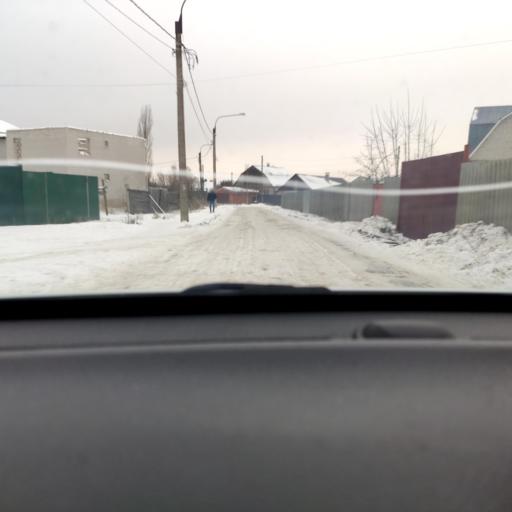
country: RU
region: Voronezj
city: Somovo
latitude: 51.7449
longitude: 39.3573
